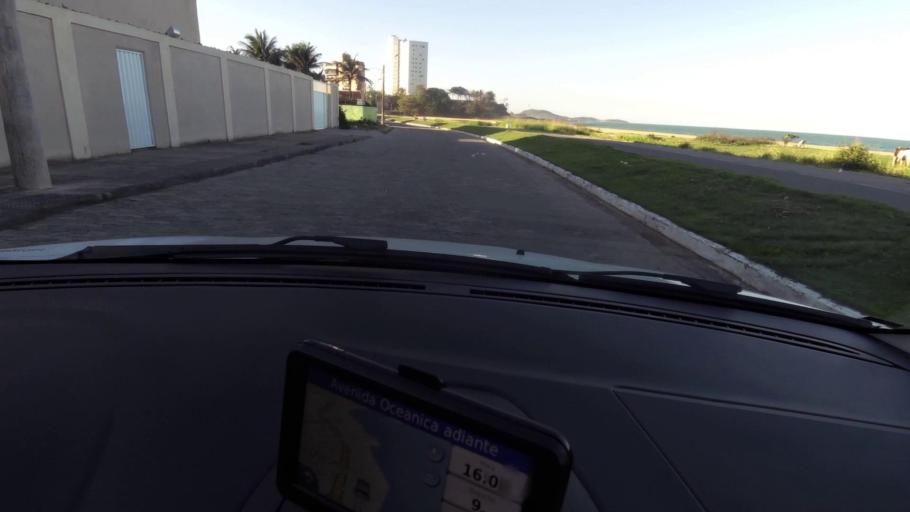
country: BR
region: Espirito Santo
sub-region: Guarapari
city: Guarapari
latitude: -20.6821
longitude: -40.5047
